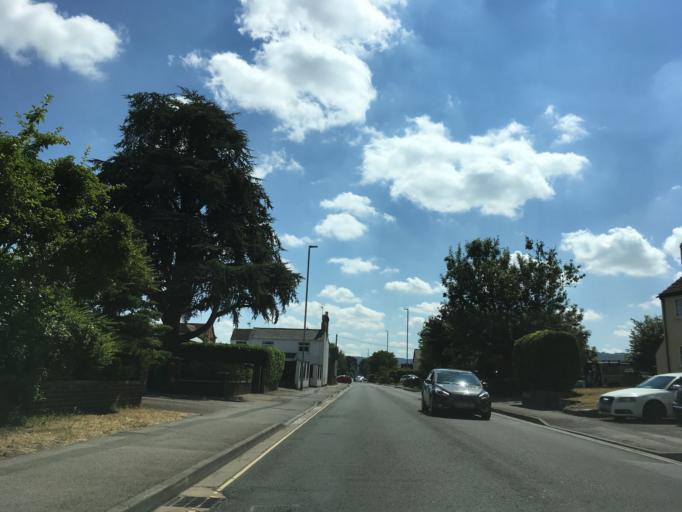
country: GB
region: England
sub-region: Gloucestershire
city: Barnwood
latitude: 51.8585
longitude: -2.1966
